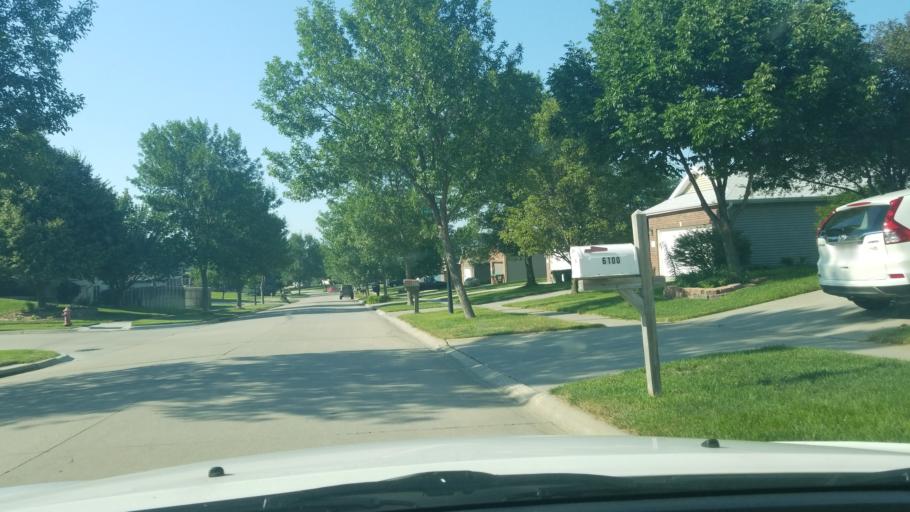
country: US
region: Nebraska
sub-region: Lancaster County
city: Lincoln
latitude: 40.7515
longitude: -96.6109
